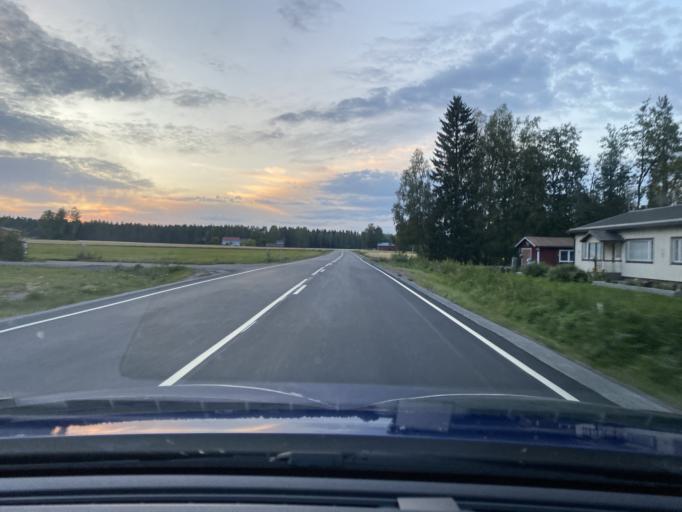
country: FI
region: Satakunta
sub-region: Pohjois-Satakunta
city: Honkajoki
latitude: 62.0813
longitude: 22.2504
